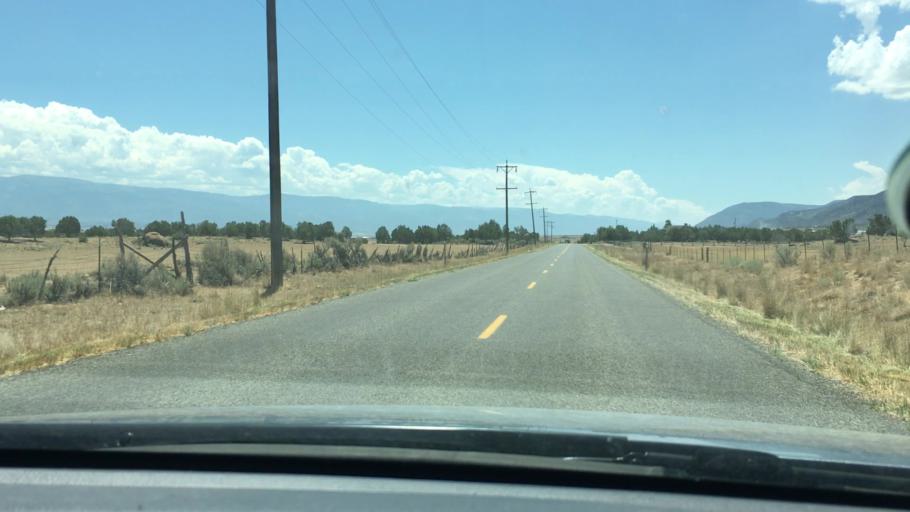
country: US
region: Utah
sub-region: Sanpete County
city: Fountain Green
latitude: 39.5945
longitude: -111.6429
